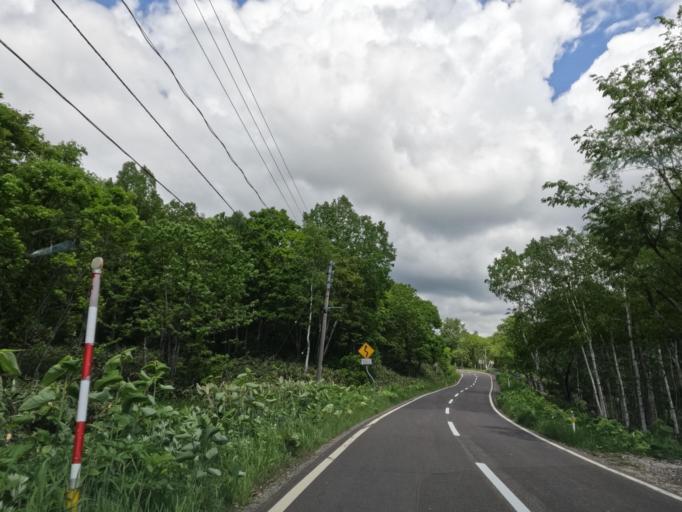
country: JP
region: Hokkaido
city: Takikawa
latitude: 43.5548
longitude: 141.6688
